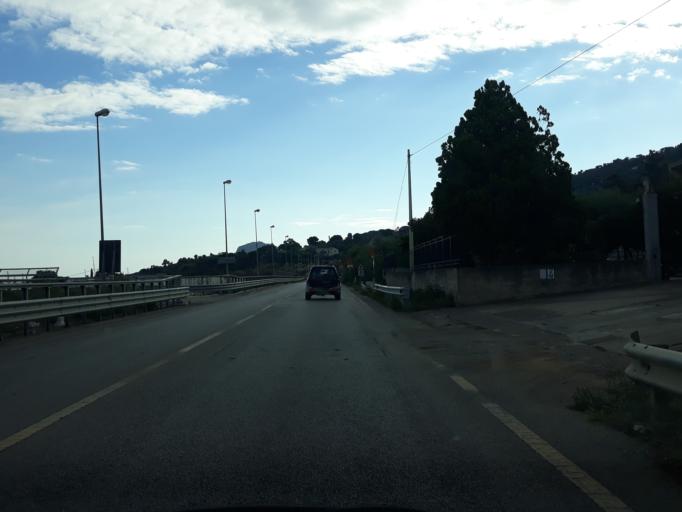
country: IT
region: Sicily
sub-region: Palermo
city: Cefalu
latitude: 38.0261
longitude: 13.9816
